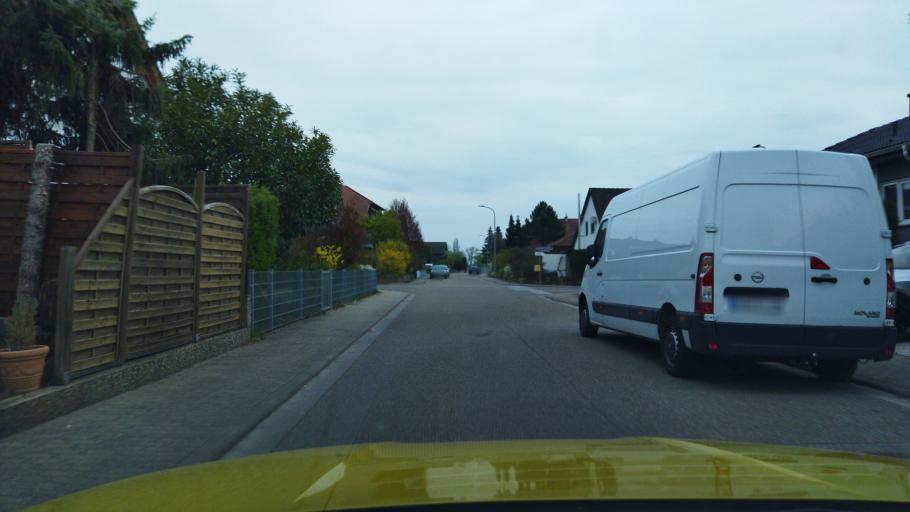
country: DE
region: Rheinland-Pfalz
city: Hanhofen
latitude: 49.3148
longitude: 8.3485
